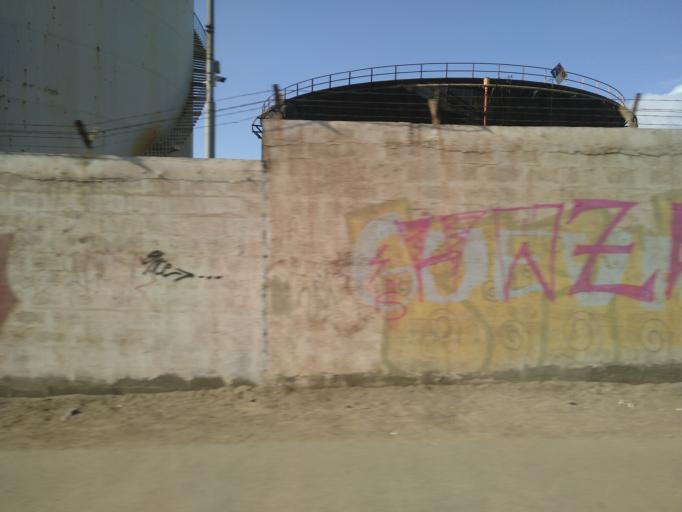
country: CL
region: Antofagasta
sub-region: Provincia de Antofagasta
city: Antofagasta
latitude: -23.6137
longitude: -70.3907
